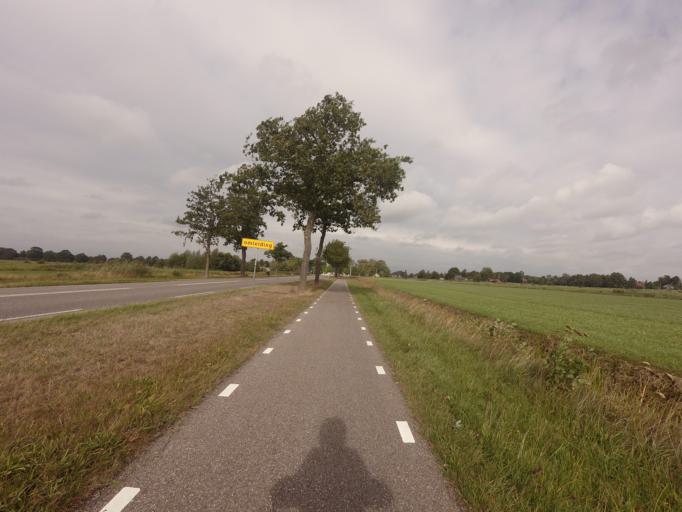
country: NL
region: Friesland
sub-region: Gemeente Opsterland
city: Gorredijk
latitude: 52.9923
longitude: 6.0822
